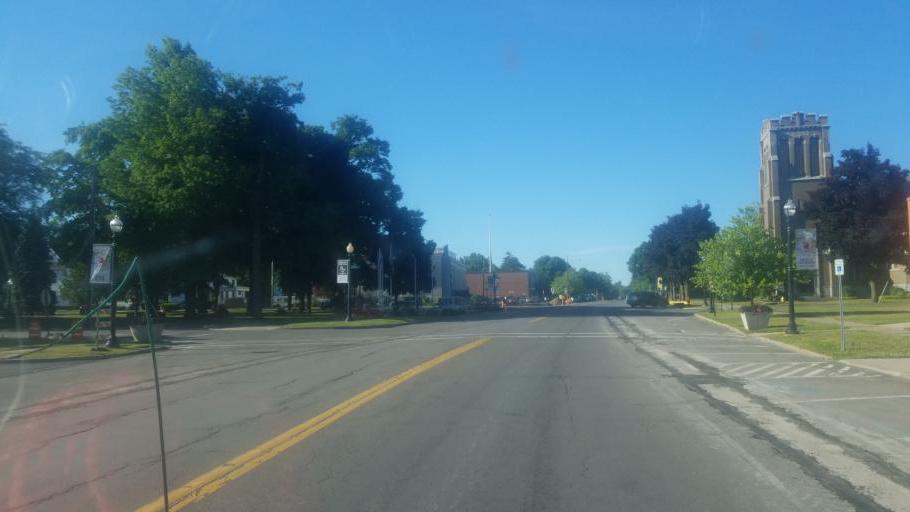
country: US
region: New York
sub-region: Wayne County
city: Newark
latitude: 43.0450
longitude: -77.0952
